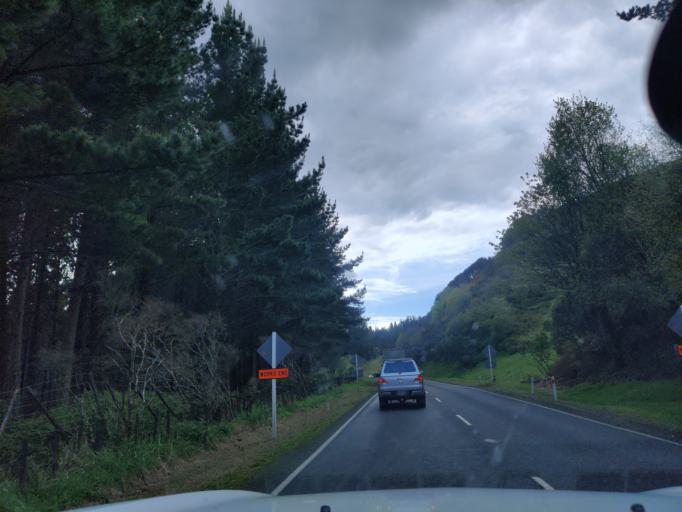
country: NZ
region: Waikato
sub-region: Otorohanga District
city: Otorohanga
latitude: -38.6468
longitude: 175.2076
